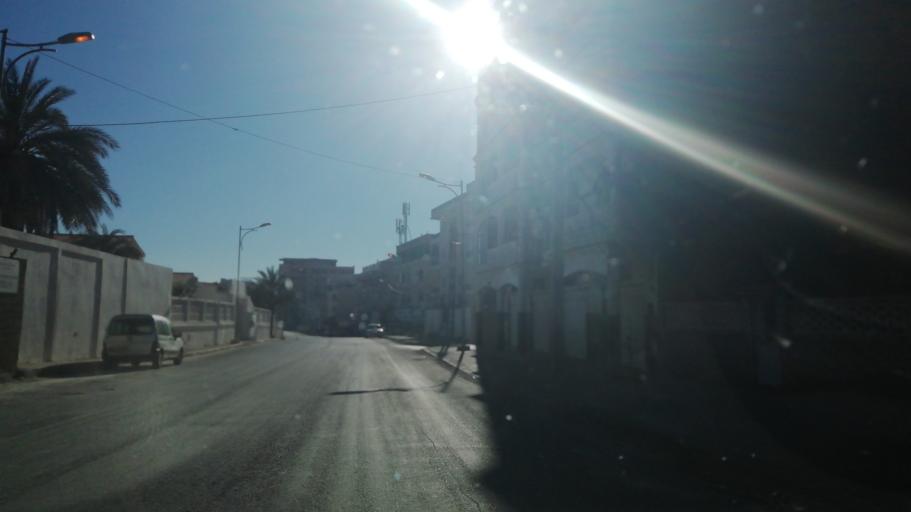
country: DZ
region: Oran
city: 'Ain el Turk
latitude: 35.7533
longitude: -0.7838
